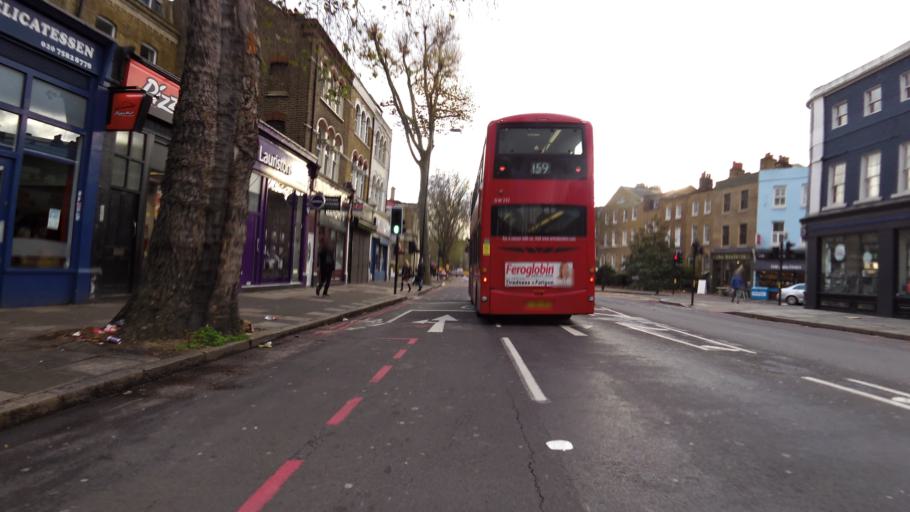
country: GB
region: England
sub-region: Greater London
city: Kennington
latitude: 51.4875
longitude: -0.1113
